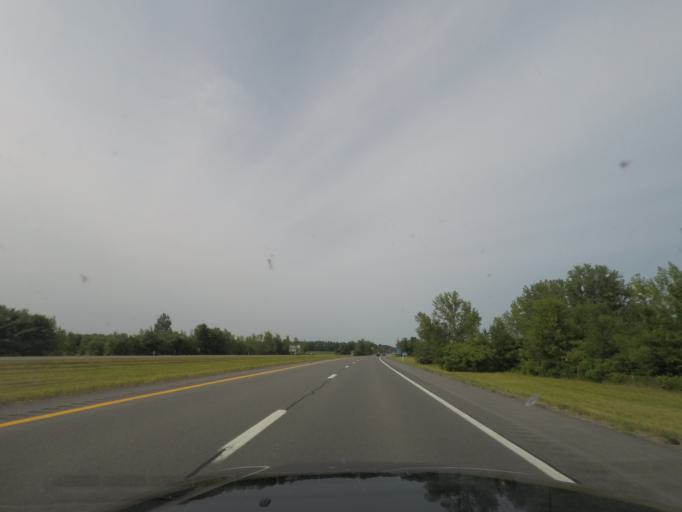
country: US
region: New York
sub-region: Clinton County
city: Peru
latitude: 44.5857
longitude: -73.5010
